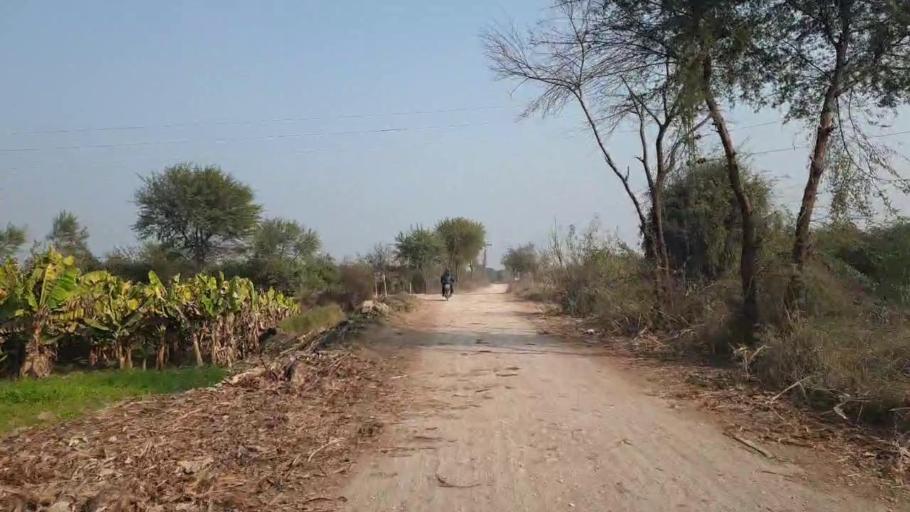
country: PK
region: Sindh
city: Bhit Shah
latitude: 25.8848
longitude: 68.4751
